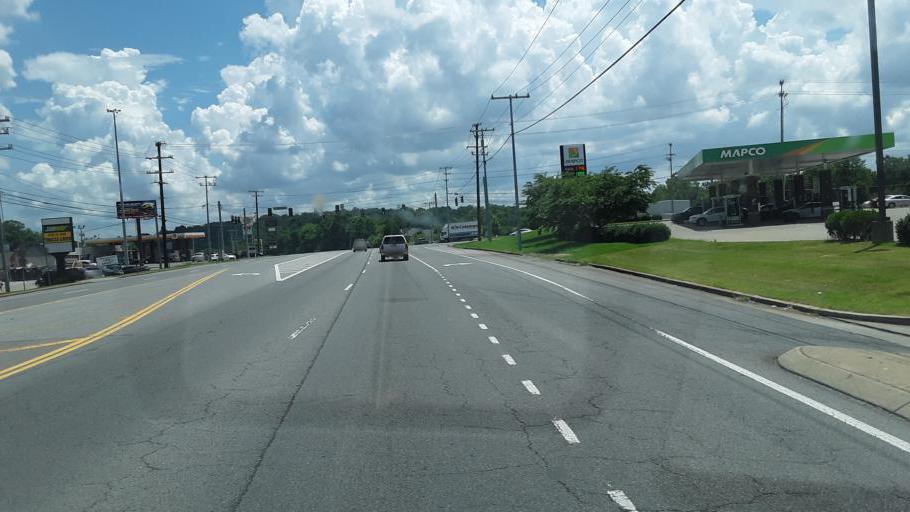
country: US
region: Kentucky
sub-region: Christian County
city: Oak Grove
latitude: 36.6260
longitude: -87.3714
